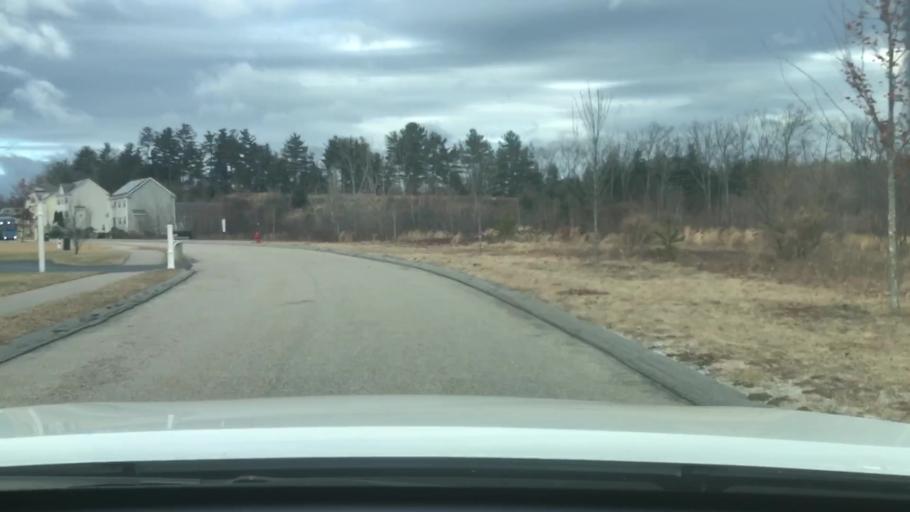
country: US
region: Rhode Island
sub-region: Providence County
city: Woonsocket
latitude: 42.0360
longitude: -71.5091
